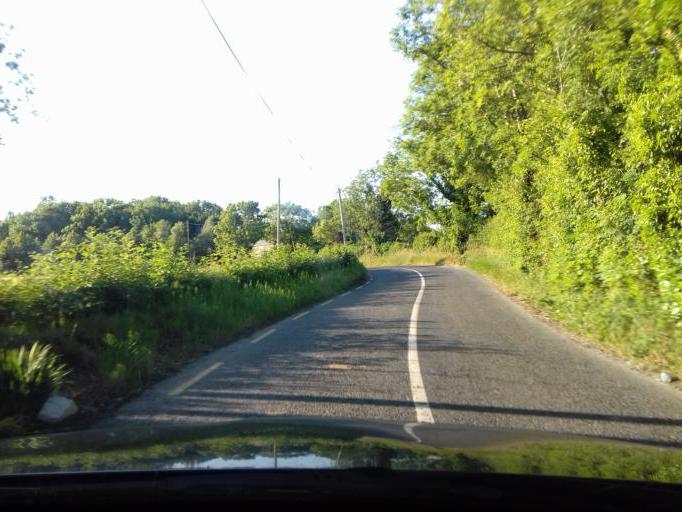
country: IE
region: Leinster
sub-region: An Mhi
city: Ashbourne
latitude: 53.5492
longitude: -6.3752
